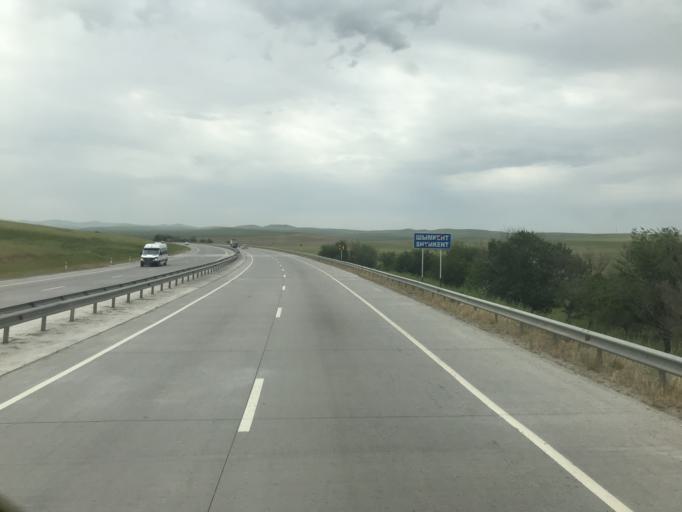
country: KZ
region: Ongtustik Qazaqstan
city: Shymkent
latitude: 42.1749
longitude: 69.4913
